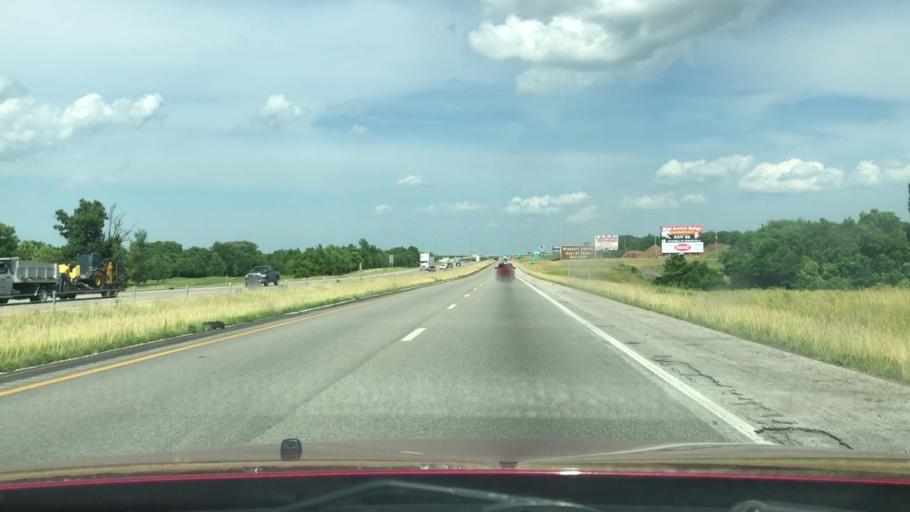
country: US
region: Missouri
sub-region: Greene County
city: Springfield
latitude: 37.2501
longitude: -93.2396
